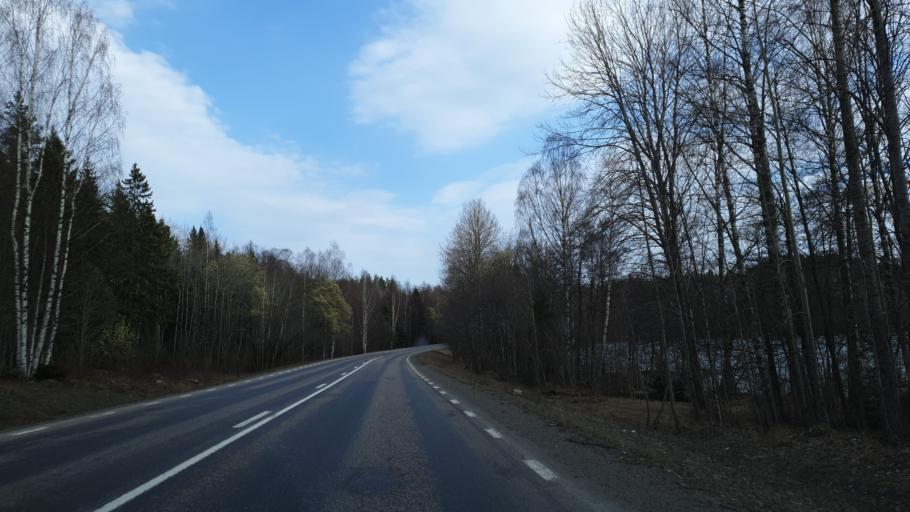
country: SE
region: Gaevleborg
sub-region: Hudiksvalls Kommun
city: Iggesund
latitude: 61.6489
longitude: 17.0427
